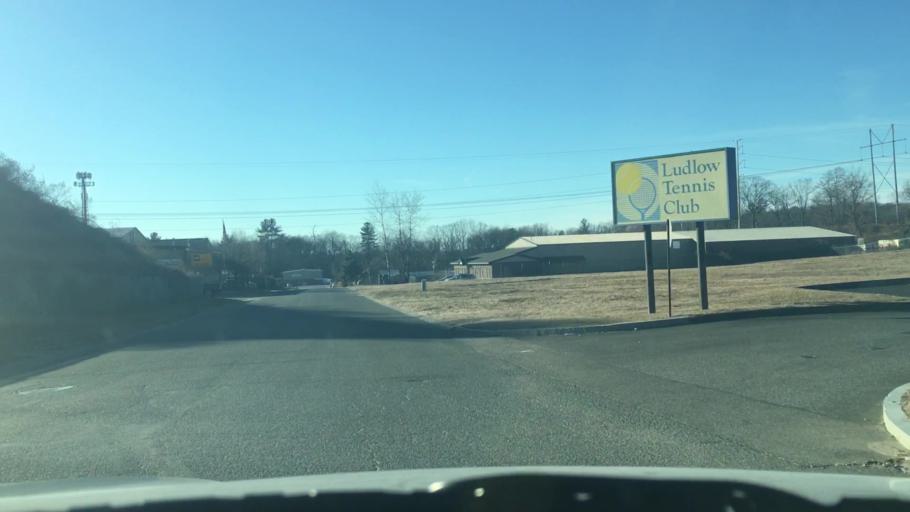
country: US
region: Massachusetts
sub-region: Hampden County
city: Ludlow
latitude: 42.1730
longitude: -72.4468
